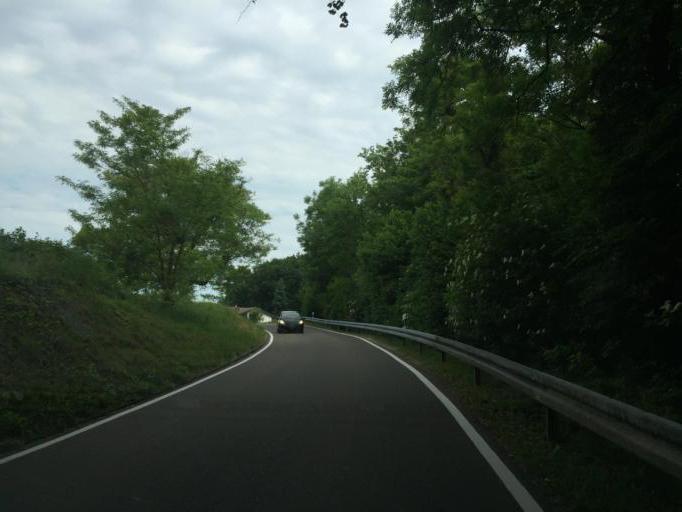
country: CH
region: Zurich
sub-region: Bezirk Andelfingen
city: Dachsen
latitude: 47.6530
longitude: 8.6017
